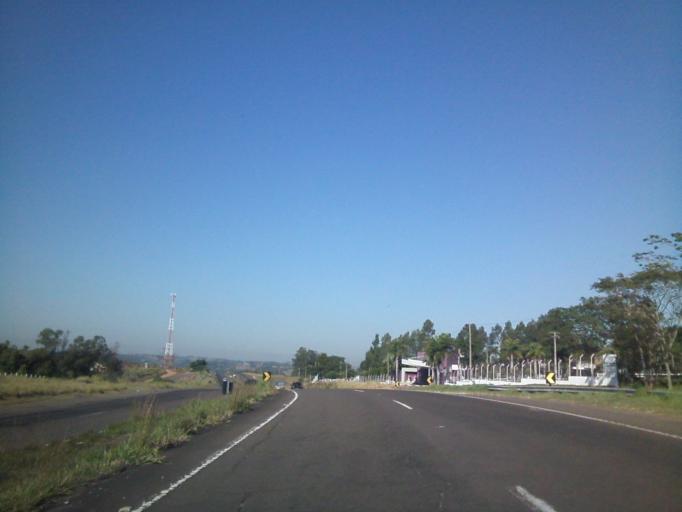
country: BR
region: Sao Paulo
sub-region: Presidente Prudente
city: Presidente Prudente
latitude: -22.1878
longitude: -51.4316
